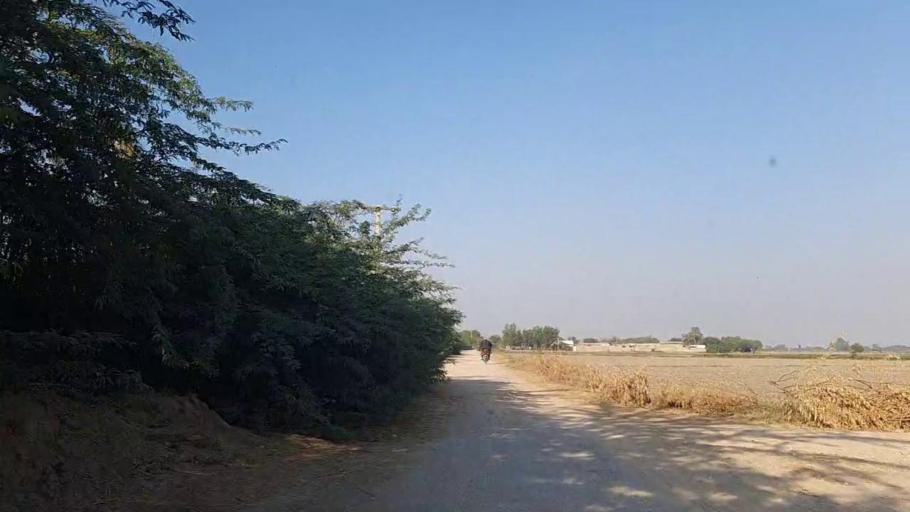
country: PK
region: Sindh
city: Thatta
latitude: 24.7561
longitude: 67.9616
